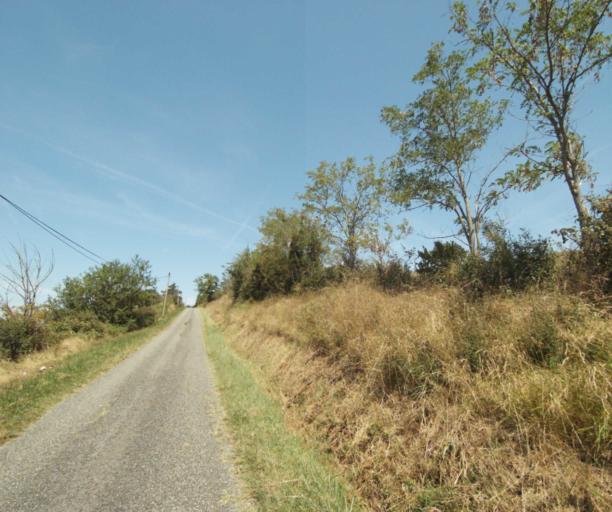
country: FR
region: Midi-Pyrenees
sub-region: Departement de l'Ariege
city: Lezat-sur-Leze
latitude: 43.3081
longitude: 1.3461
